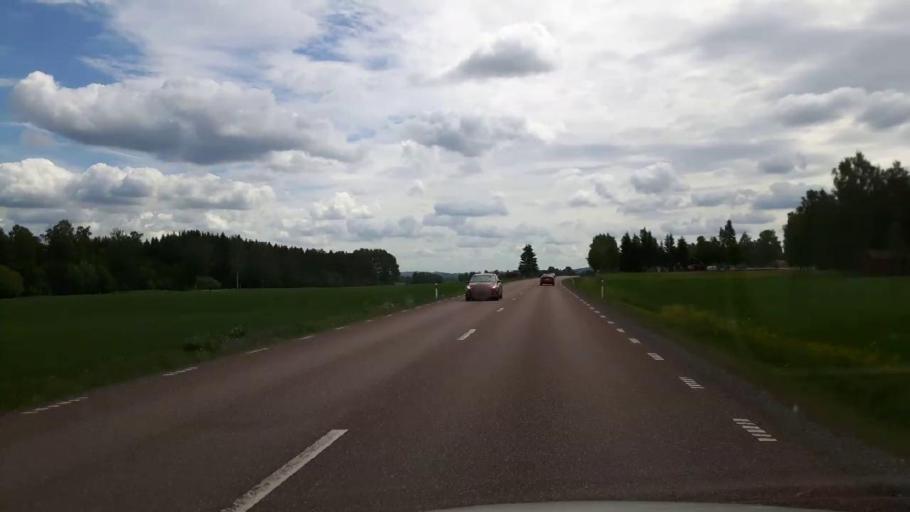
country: SE
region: Dalarna
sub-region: Hedemora Kommun
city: Hedemora
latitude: 60.3121
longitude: 15.9671
